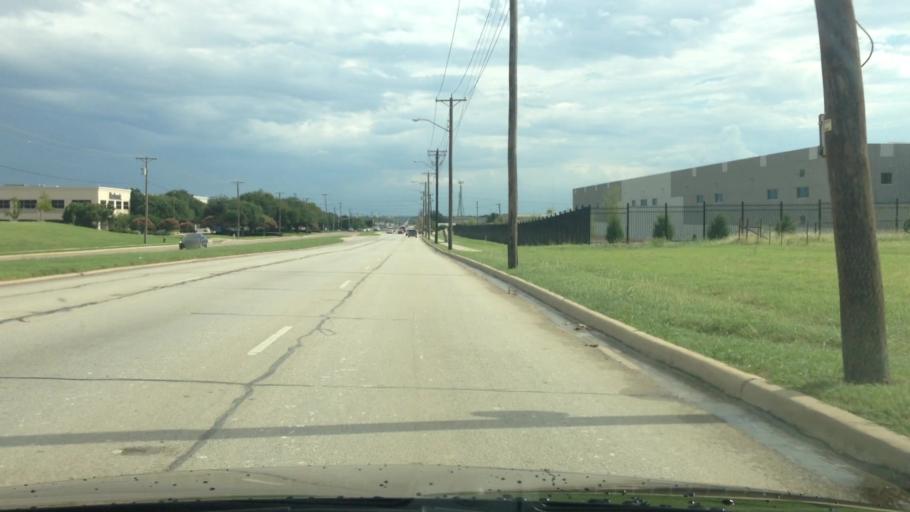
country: US
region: Texas
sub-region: Tarrant County
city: Haltom City
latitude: 32.8279
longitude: -97.2907
